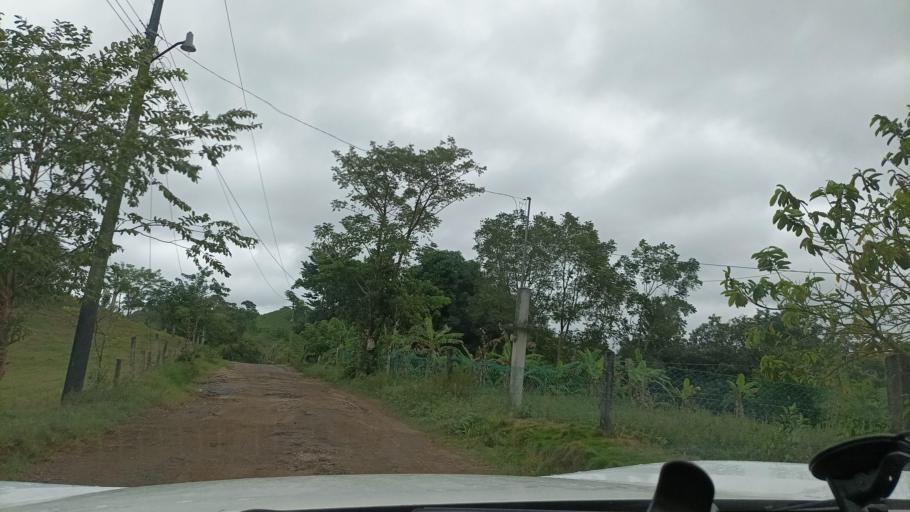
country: MX
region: Veracruz
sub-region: Moloacan
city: Cuichapa
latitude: 17.7875
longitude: -94.3871
